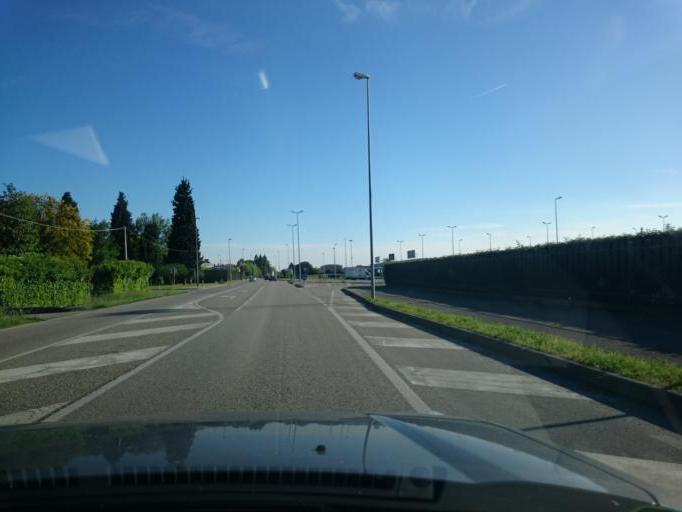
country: IT
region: Veneto
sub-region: Provincia di Venezia
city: Caselle
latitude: 45.4947
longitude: 12.0073
